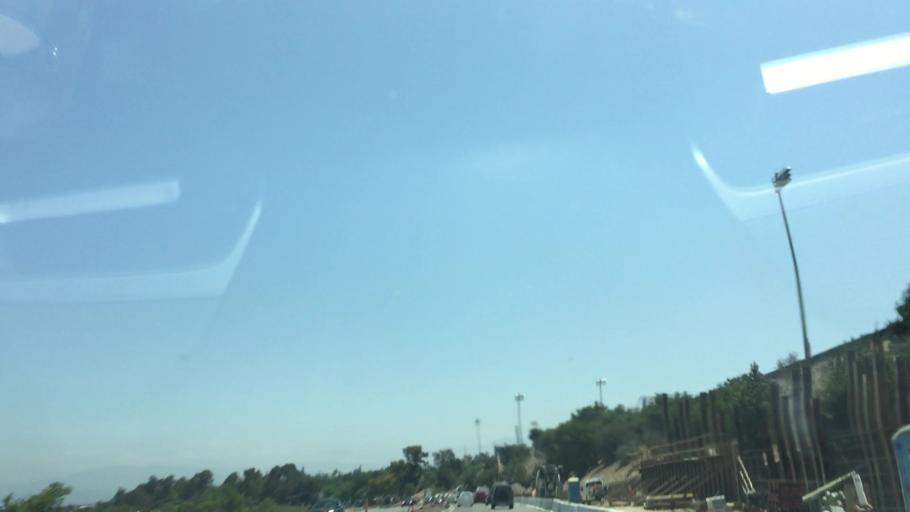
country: US
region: California
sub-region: Orange County
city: Irvine
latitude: 33.6507
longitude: -117.8507
